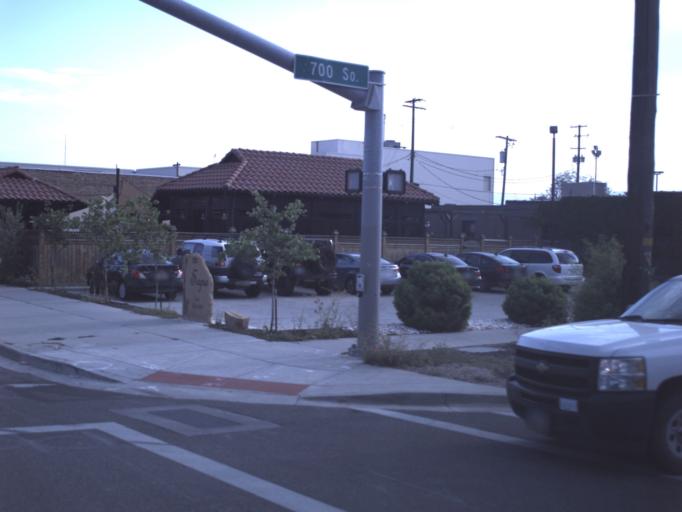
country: US
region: Utah
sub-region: Salt Lake County
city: Salt Lake City
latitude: 40.7541
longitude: -111.8884
